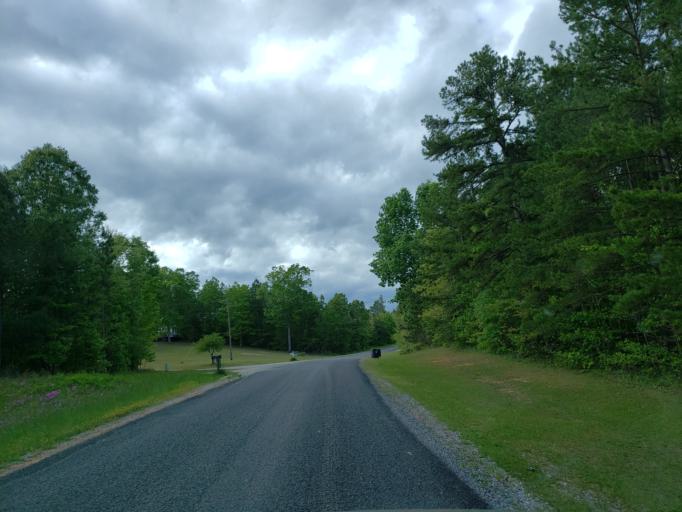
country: US
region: Georgia
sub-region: Haralson County
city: Tallapoosa
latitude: 33.8100
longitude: -85.3863
